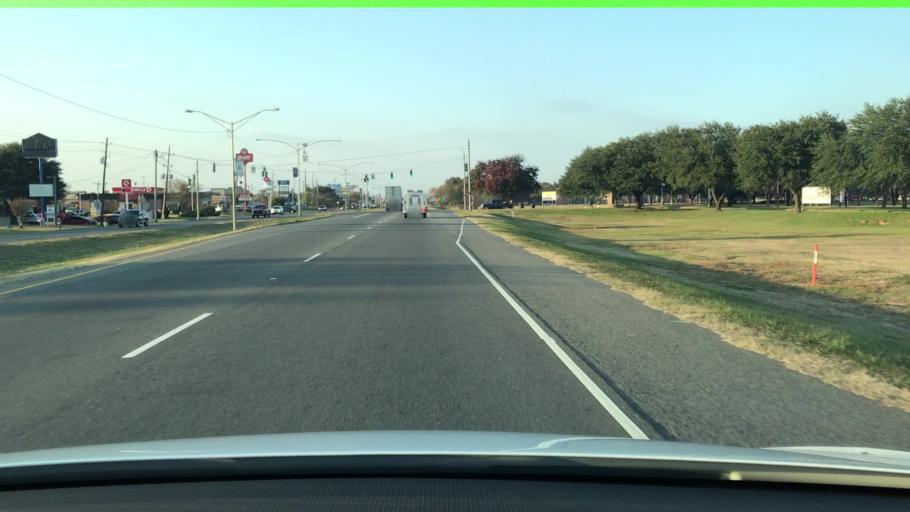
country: US
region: Louisiana
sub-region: Bossier Parish
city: Bossier City
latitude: 32.4256
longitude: -93.7081
